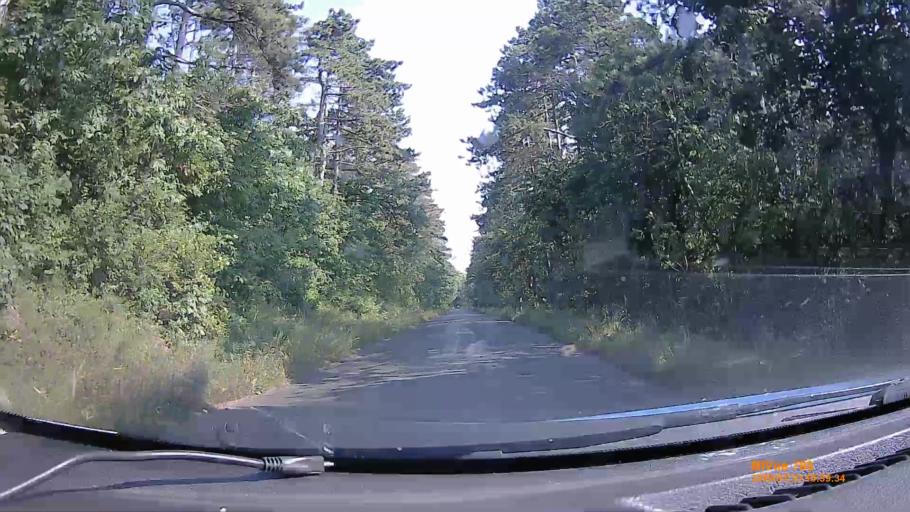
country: HU
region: Baranya
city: Pecs
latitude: 46.1098
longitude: 18.1983
